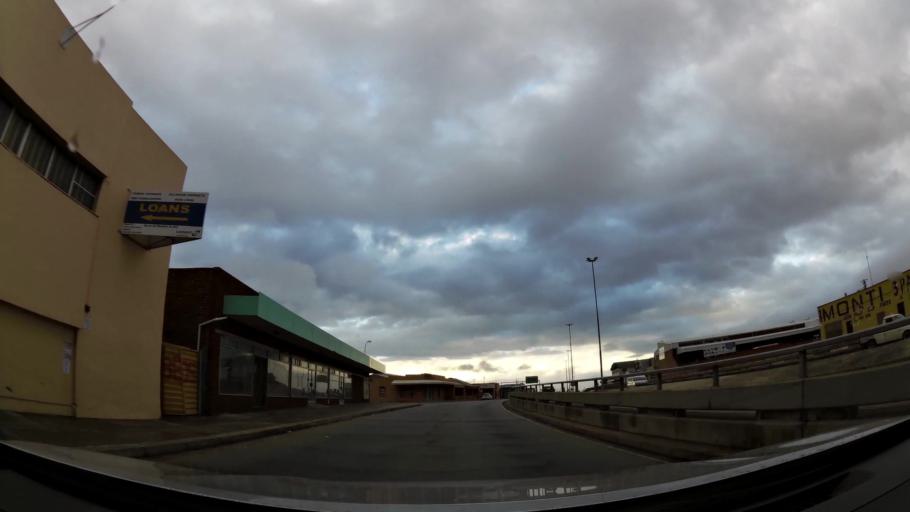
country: ZA
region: Eastern Cape
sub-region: Nelson Mandela Bay Metropolitan Municipality
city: Port Elizabeth
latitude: -33.9212
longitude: 25.5923
